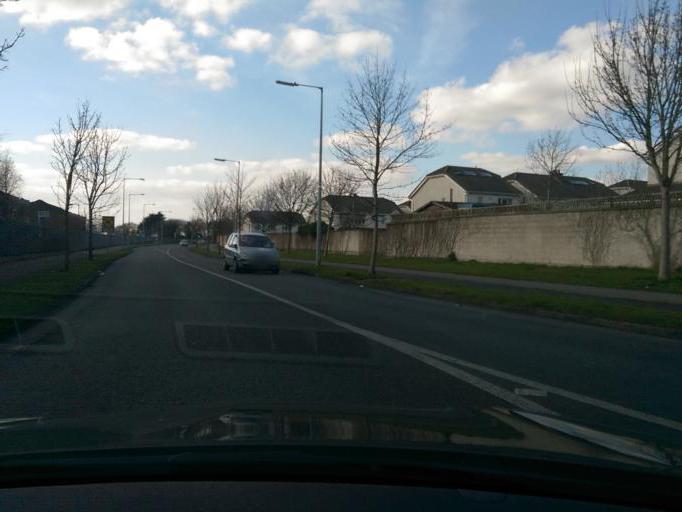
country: IE
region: Leinster
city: Clondalkin
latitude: 53.3419
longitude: -6.4145
